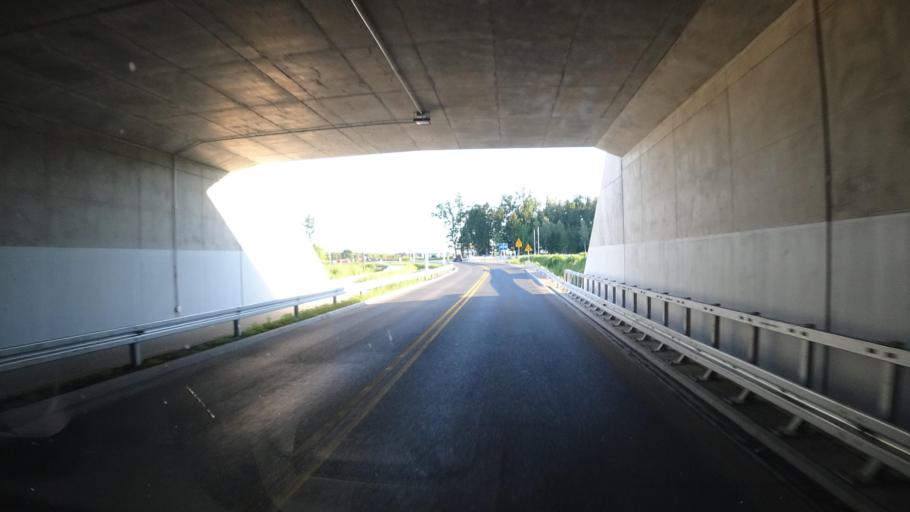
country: PL
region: Warmian-Masurian Voivodeship
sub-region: Powiat elcki
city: Elk
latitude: 53.8388
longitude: 22.4166
